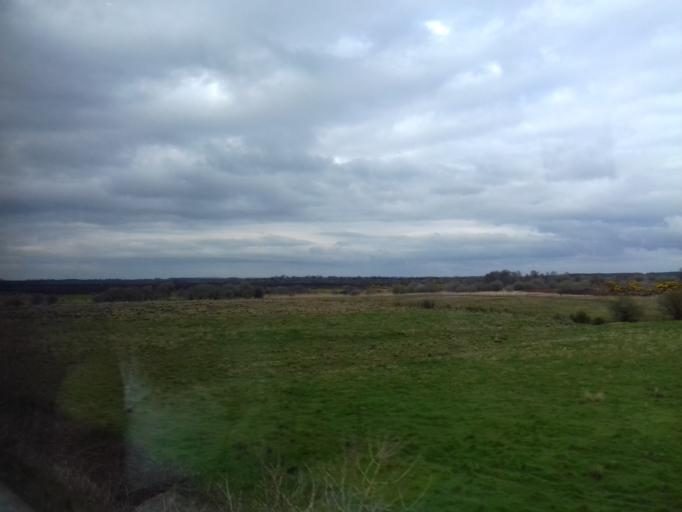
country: IE
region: Leinster
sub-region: An Iarmhi
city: Castlepollard
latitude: 53.6518
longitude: -7.4323
